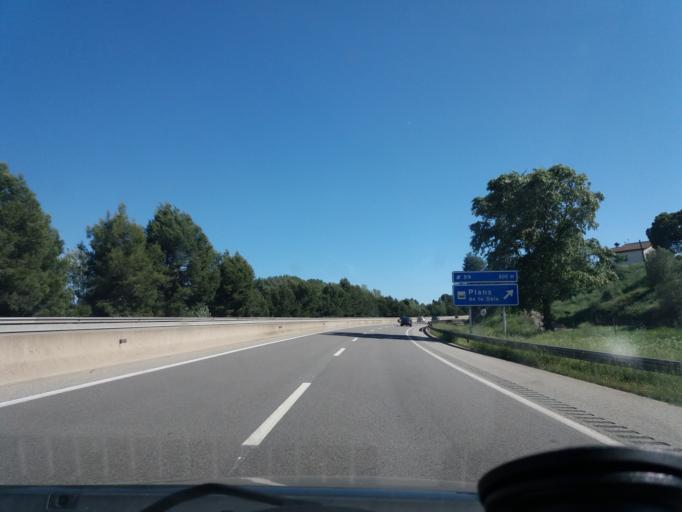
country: ES
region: Catalonia
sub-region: Provincia de Barcelona
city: Sallent
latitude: 41.7970
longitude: 1.8988
